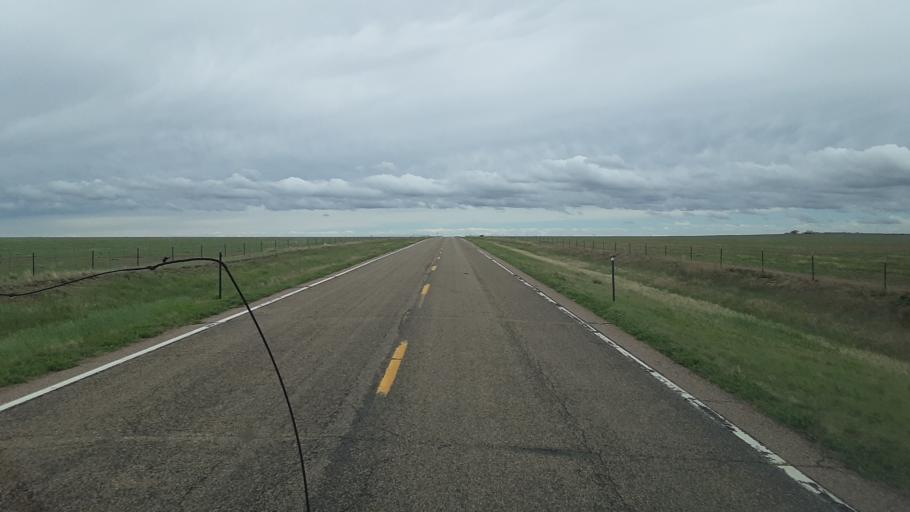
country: US
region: Colorado
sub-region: Lincoln County
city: Limon
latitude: 38.8490
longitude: -103.7975
